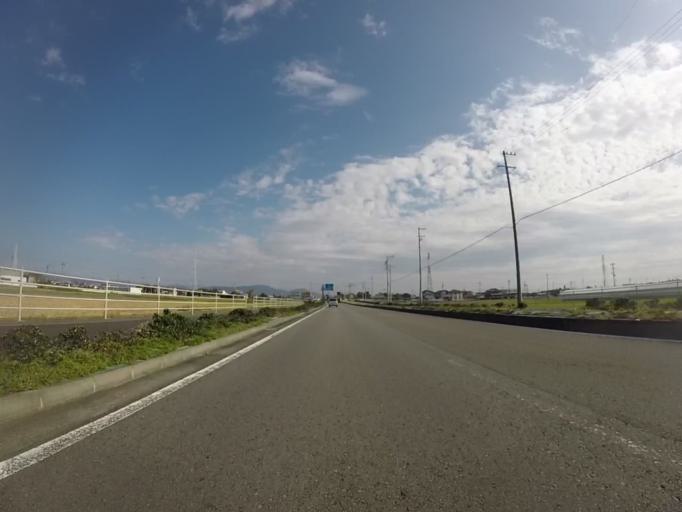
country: JP
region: Shizuoka
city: Fujieda
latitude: 34.8137
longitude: 138.2531
